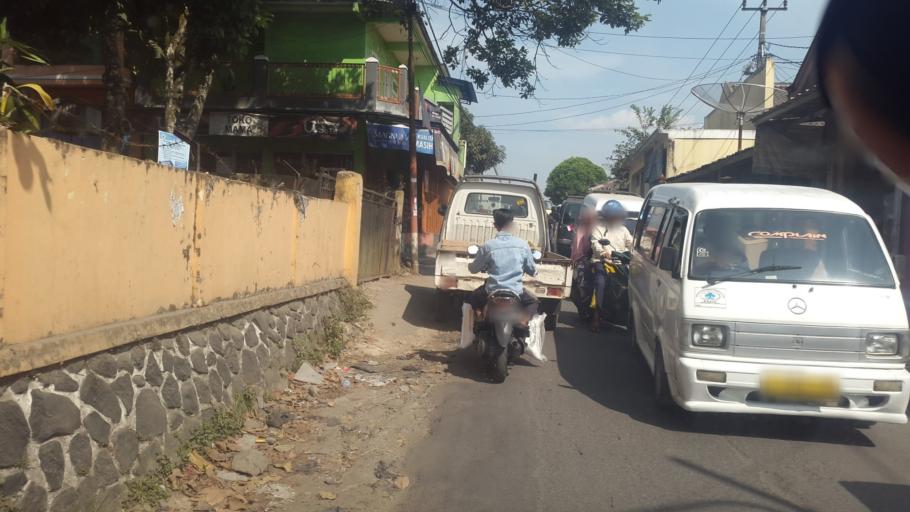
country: ID
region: West Java
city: Cicurug
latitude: -6.7991
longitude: 106.7572
